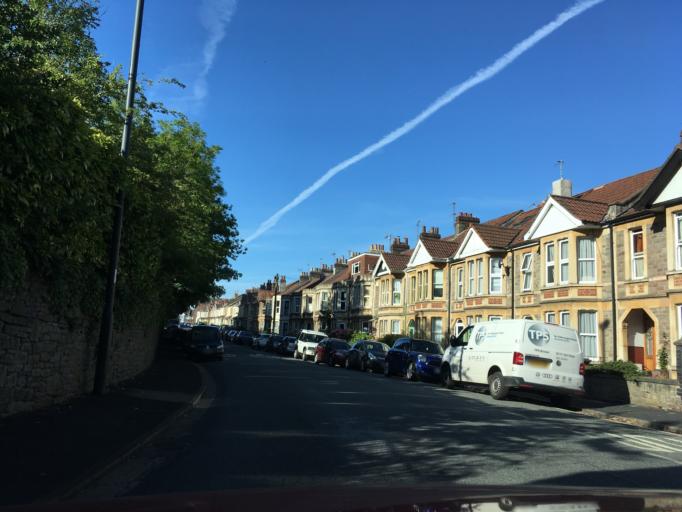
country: GB
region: England
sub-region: Bath and North East Somerset
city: Whitchurch
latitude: 51.4423
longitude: -2.5507
